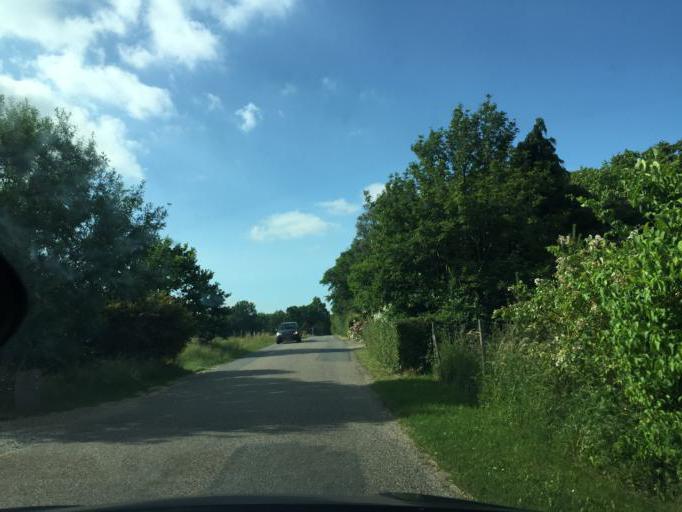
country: DK
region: South Denmark
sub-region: Faaborg-Midtfyn Kommune
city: Arslev
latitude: 55.3219
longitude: 10.5279
